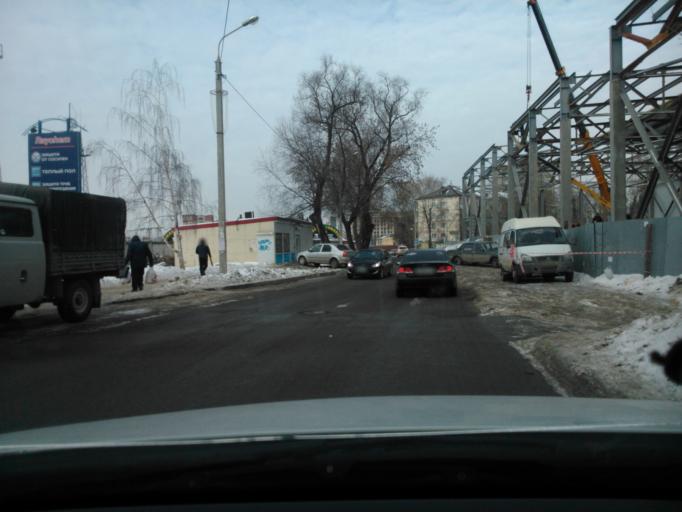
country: RU
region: Perm
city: Perm
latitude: 58.0001
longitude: 56.2330
